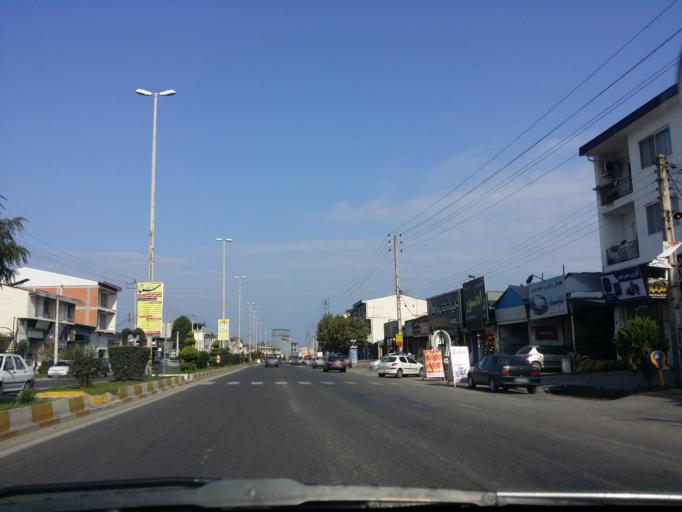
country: IR
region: Mazandaran
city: Chalus
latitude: 36.6766
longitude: 51.4041
